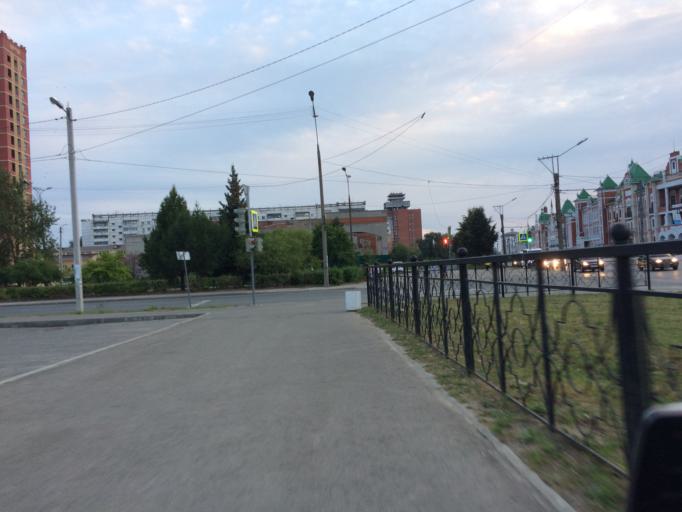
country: RU
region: Mariy-El
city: Yoshkar-Ola
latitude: 56.6327
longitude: 47.9103
